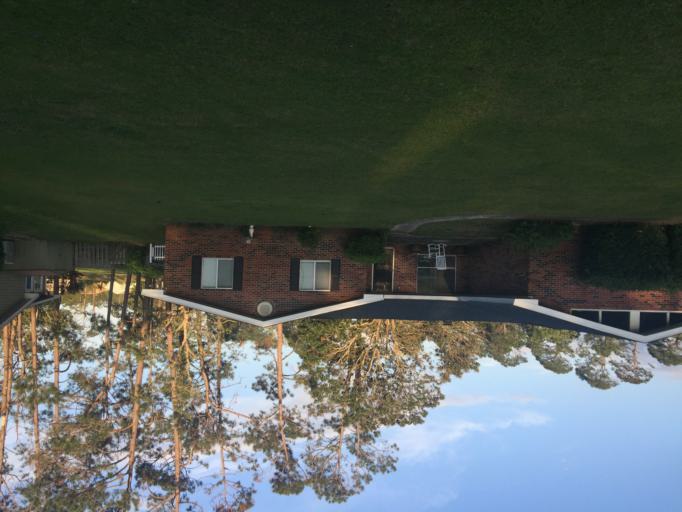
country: US
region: Florida
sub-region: Bay County
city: Panama City Beach
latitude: 30.2155
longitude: -85.8446
